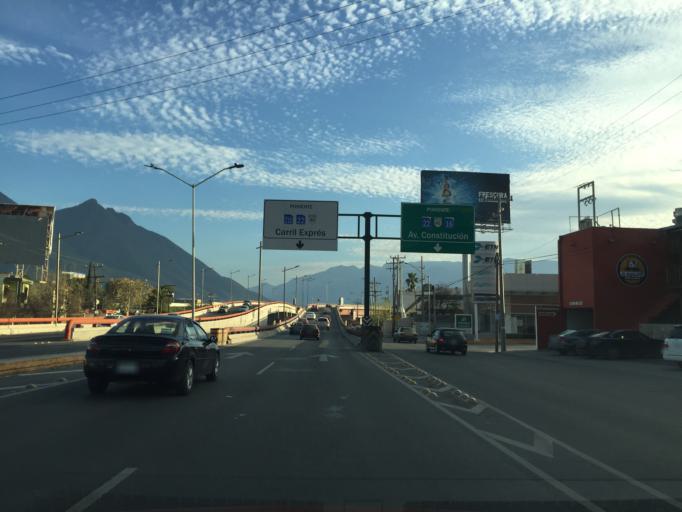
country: MX
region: Nuevo Leon
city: Guadalupe
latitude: 25.6849
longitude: -100.2685
